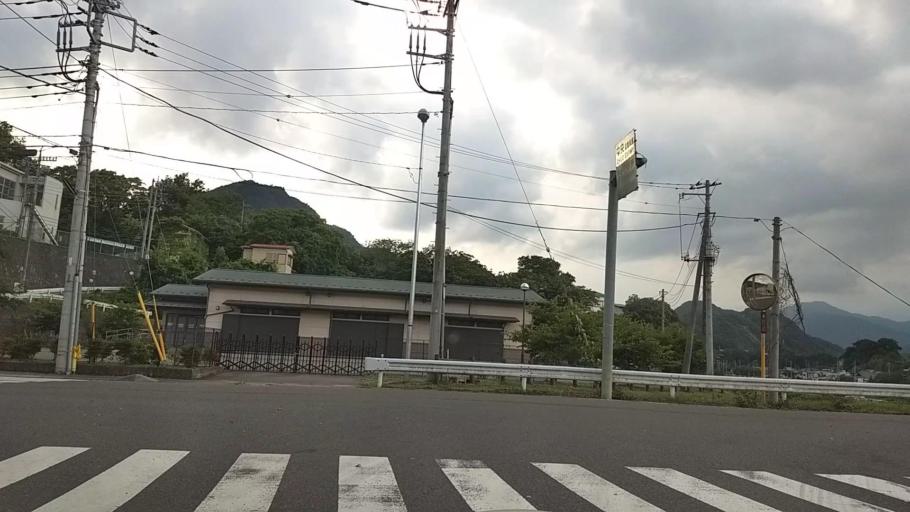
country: JP
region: Yamanashi
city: Uenohara
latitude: 35.6157
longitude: 139.1193
